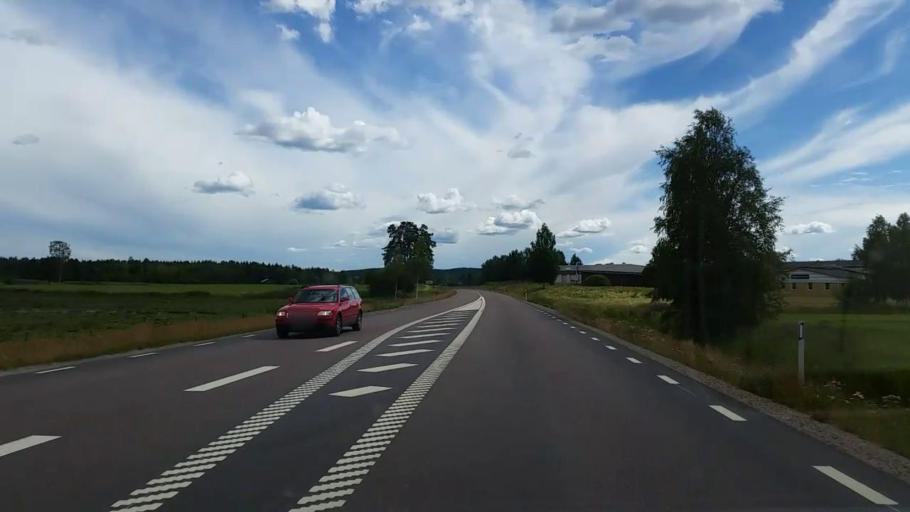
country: SE
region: Gaevleborg
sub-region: Ovanakers Kommun
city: Edsbyn
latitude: 61.3764
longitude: 15.8399
